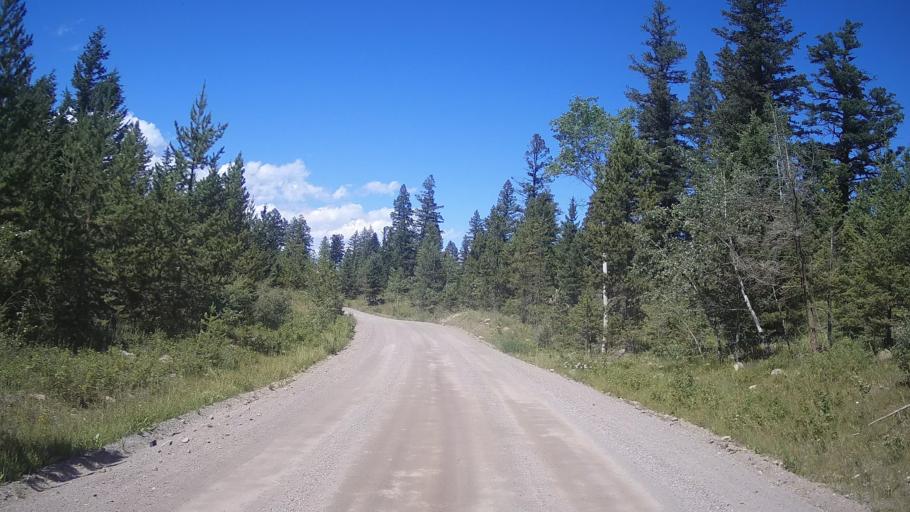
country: CA
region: British Columbia
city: Cache Creek
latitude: 51.1585
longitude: -121.5516
